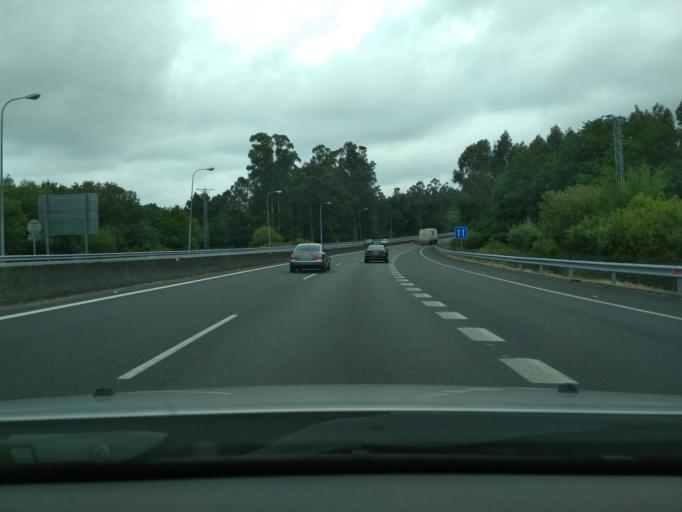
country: ES
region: Galicia
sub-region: Provincia da Coruna
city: Santiago de Compostela
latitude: 42.8090
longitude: -8.5885
